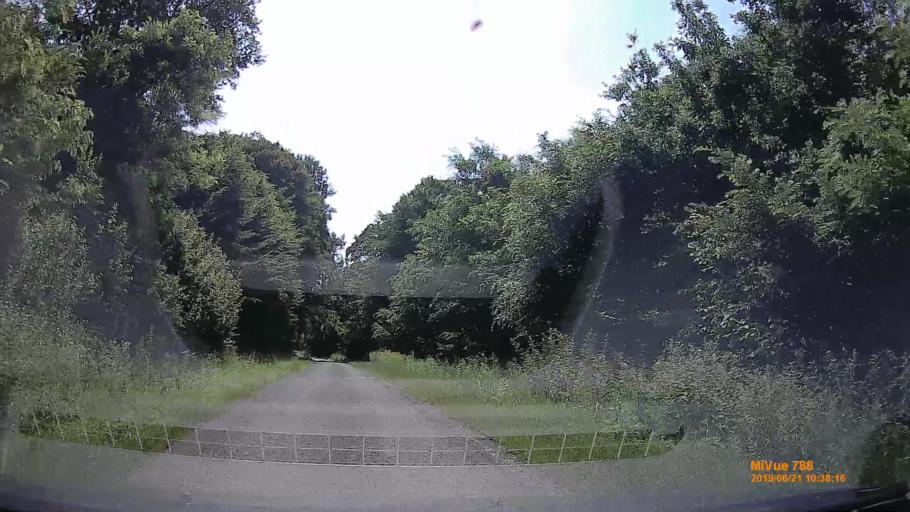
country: HU
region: Baranya
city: Buekkoesd
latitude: 46.1364
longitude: 17.9802
